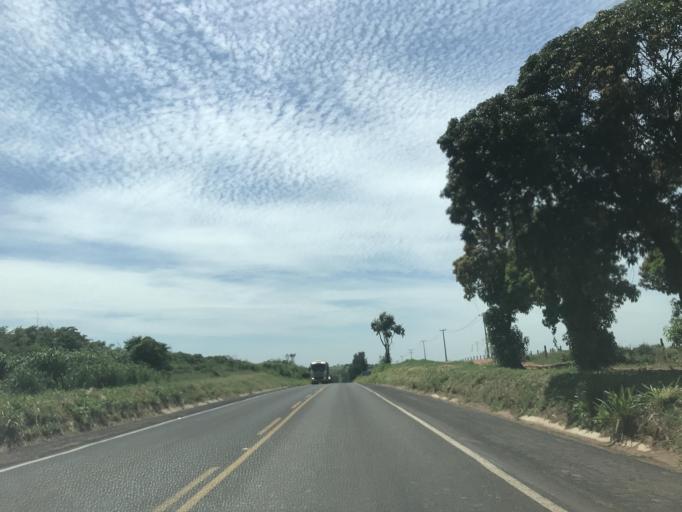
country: BR
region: Parana
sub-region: Paranavai
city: Nova Aurora
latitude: -22.9725
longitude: -52.6185
